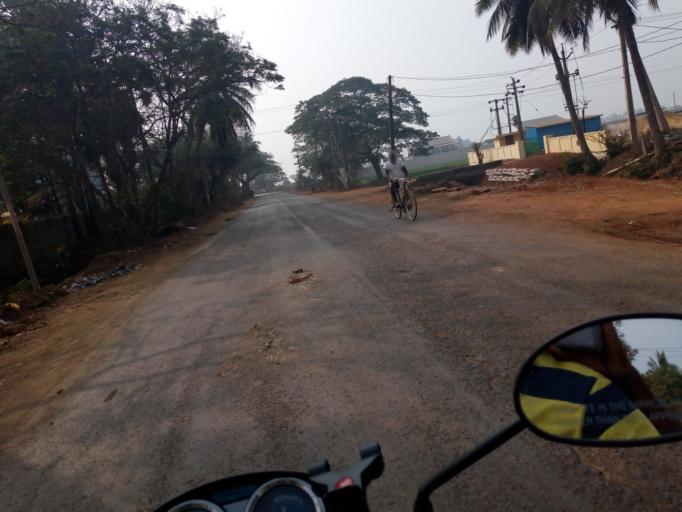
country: IN
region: Andhra Pradesh
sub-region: West Godavari
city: Tadepallegudem
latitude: 16.8103
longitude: 81.4084
